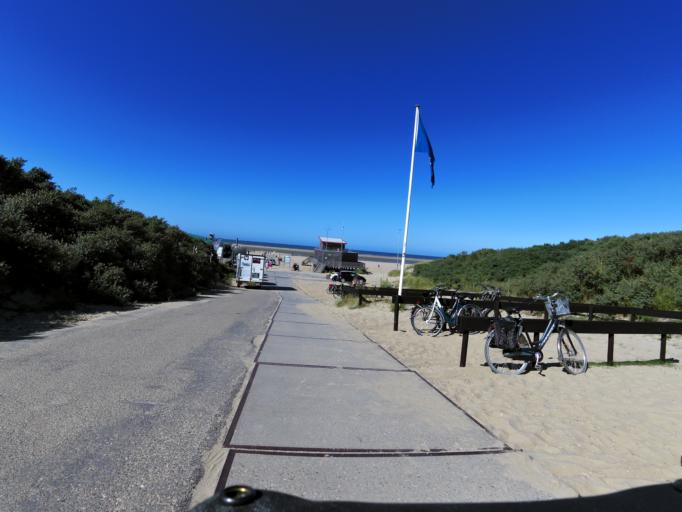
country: NL
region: South Holland
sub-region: Gemeente Goeree-Overflakkee
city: Ouddorp
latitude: 51.8270
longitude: 3.9185
